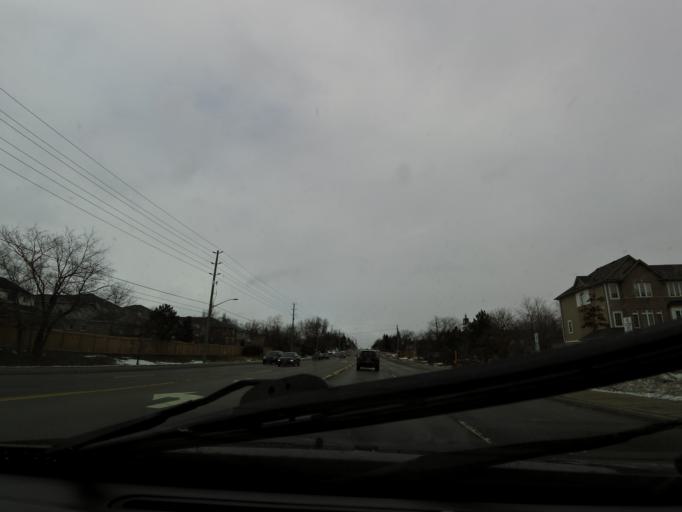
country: CA
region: Ontario
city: Hamilton
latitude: 43.3203
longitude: -79.9081
